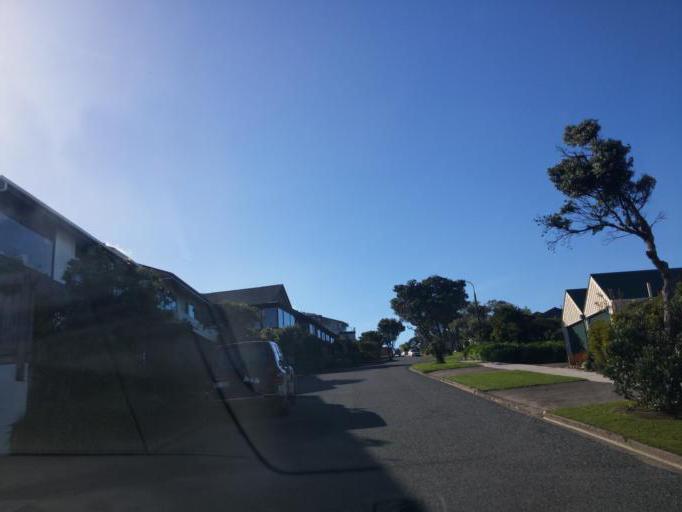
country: NZ
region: Wellington
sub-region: Wellington City
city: Wellington
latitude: -41.2544
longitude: 174.7846
